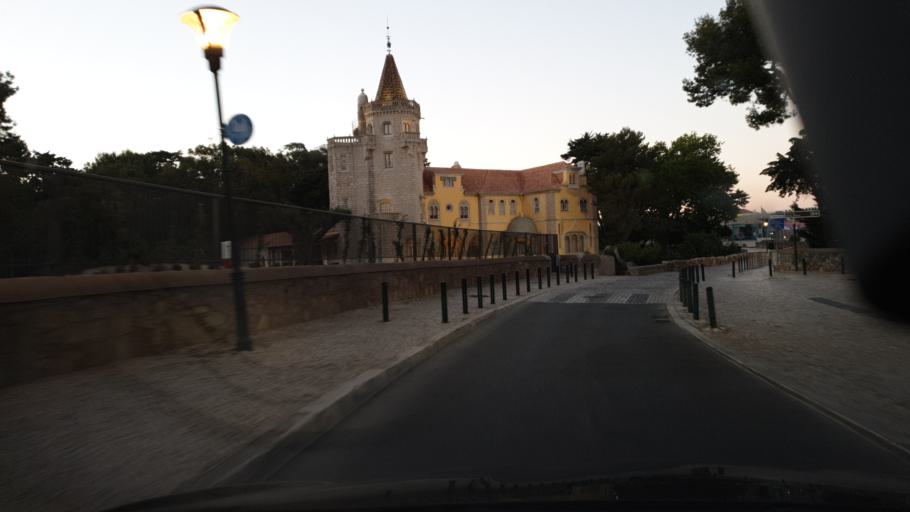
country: PT
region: Lisbon
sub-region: Cascais
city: Cascais
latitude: 38.6911
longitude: -9.4220
